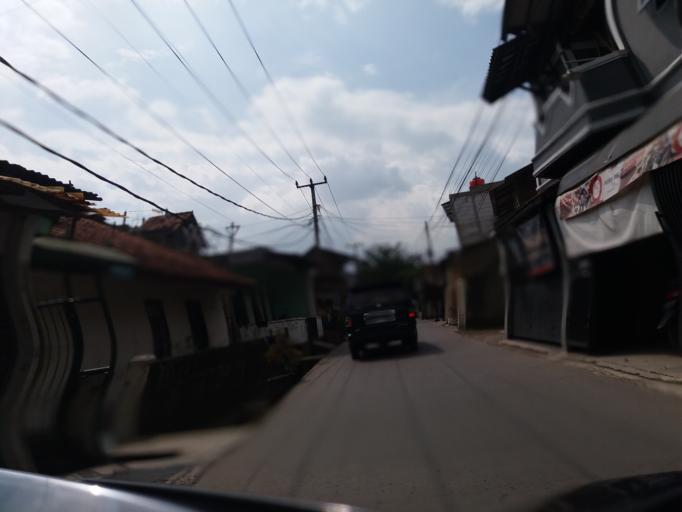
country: ID
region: West Java
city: Bandung
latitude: -6.9269
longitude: 107.6586
